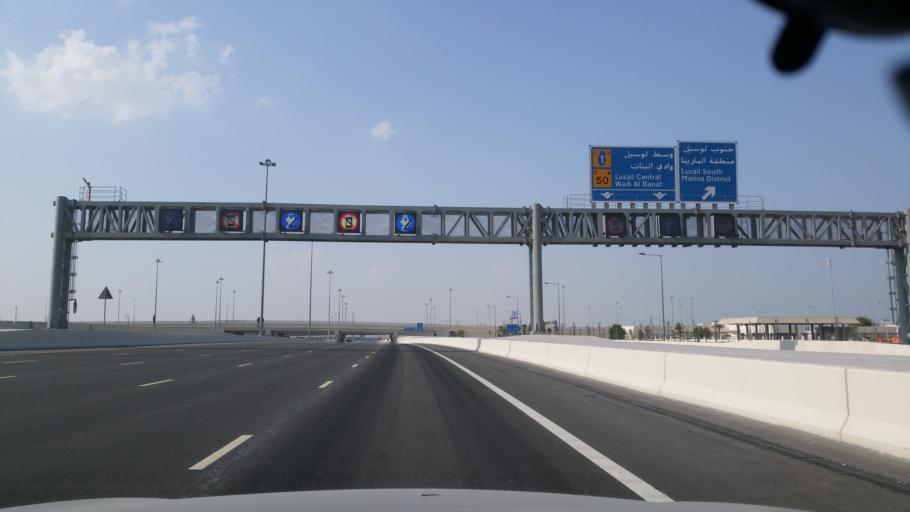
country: QA
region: Baladiyat Umm Salal
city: Umm Salal Muhammad
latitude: 25.3894
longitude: 51.4992
